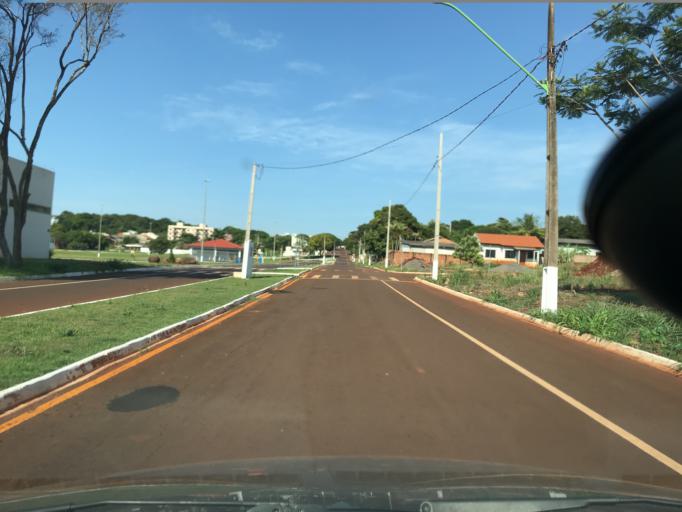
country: BR
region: Parana
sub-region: Palotina
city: Palotina
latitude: -24.2874
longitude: -53.8303
